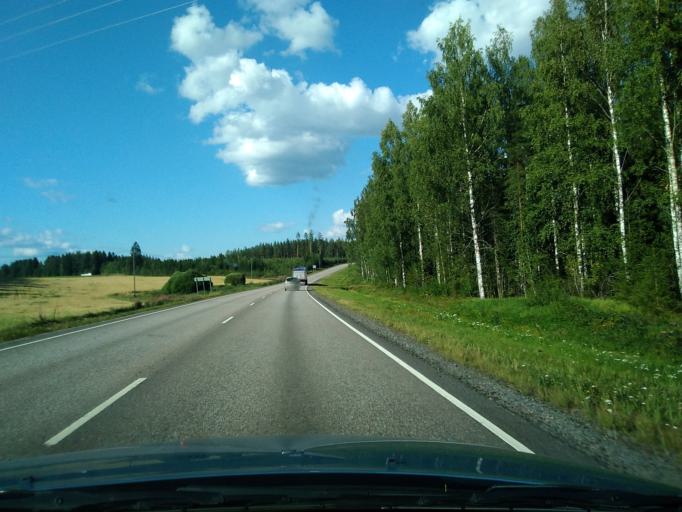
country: FI
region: Central Finland
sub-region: Keuruu
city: Keuruu
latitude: 62.1302
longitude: 24.7362
